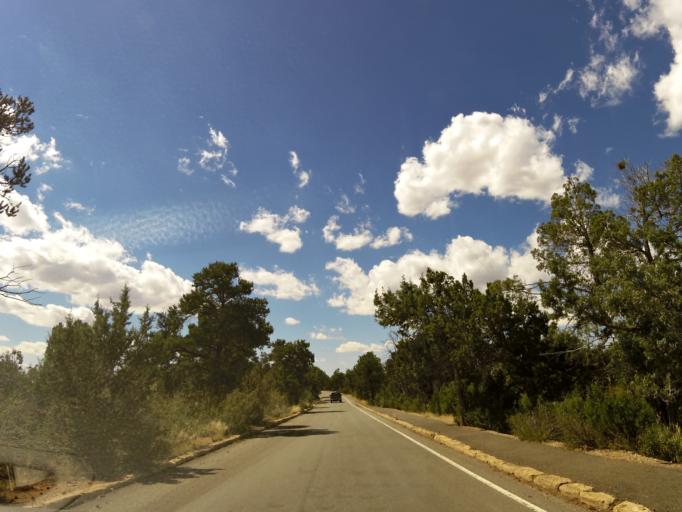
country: US
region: Colorado
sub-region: Montezuma County
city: Cortez
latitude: 37.1875
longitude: -108.4886
